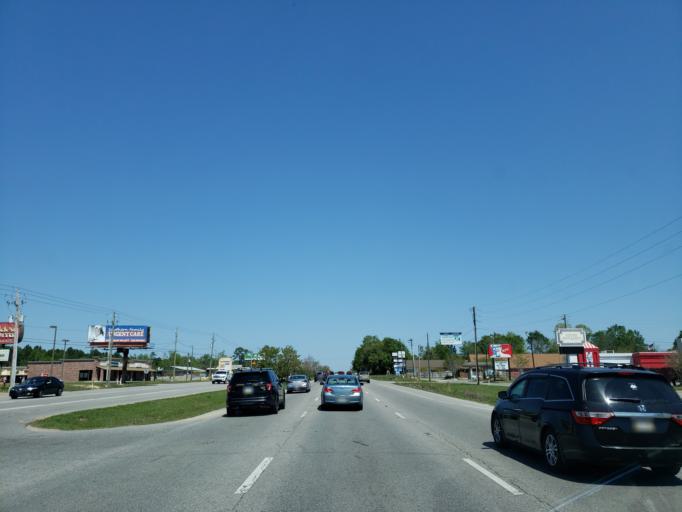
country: US
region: Mississippi
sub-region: Harrison County
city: Lyman
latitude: 30.4619
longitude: -89.1012
